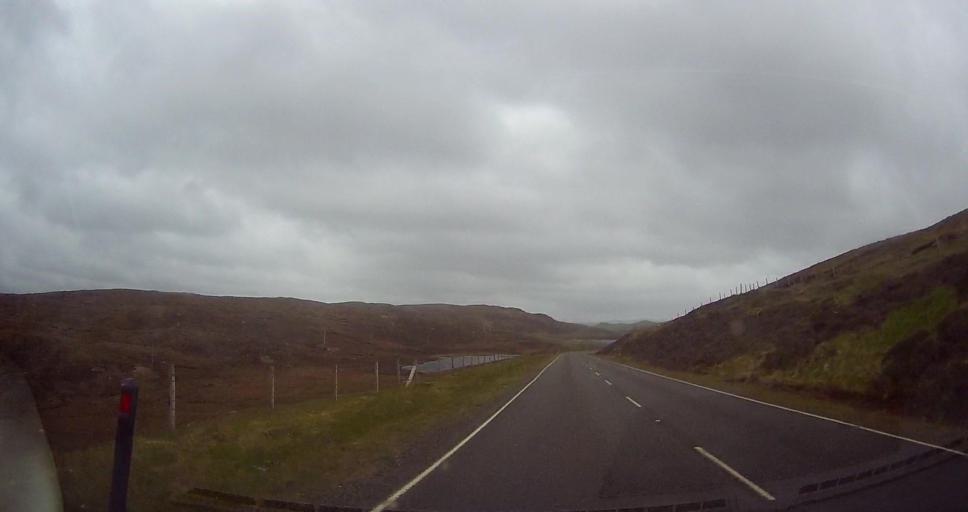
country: GB
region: Scotland
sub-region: Shetland Islands
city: Lerwick
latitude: 60.4504
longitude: -1.3955
